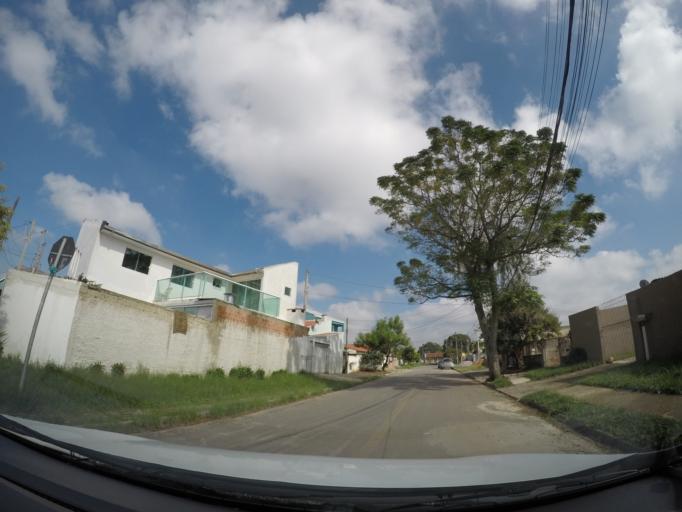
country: BR
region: Parana
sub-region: Sao Jose Dos Pinhais
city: Sao Jose dos Pinhais
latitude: -25.4961
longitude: -49.2211
